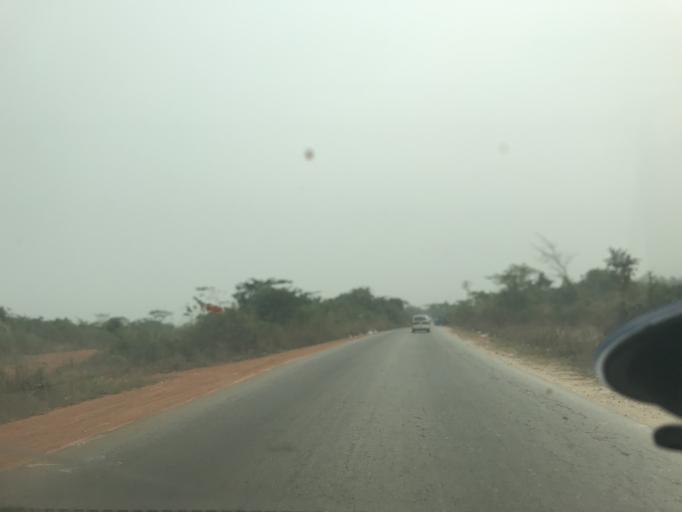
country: NG
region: Ogun
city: Ilaro
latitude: 6.8842
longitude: 3.1091
